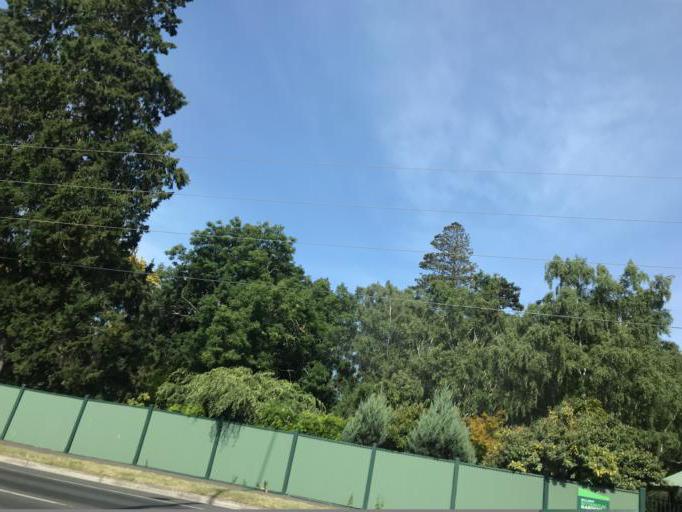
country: AU
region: Victoria
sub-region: Ballarat North
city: Newington
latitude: -37.5480
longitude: 143.8205
